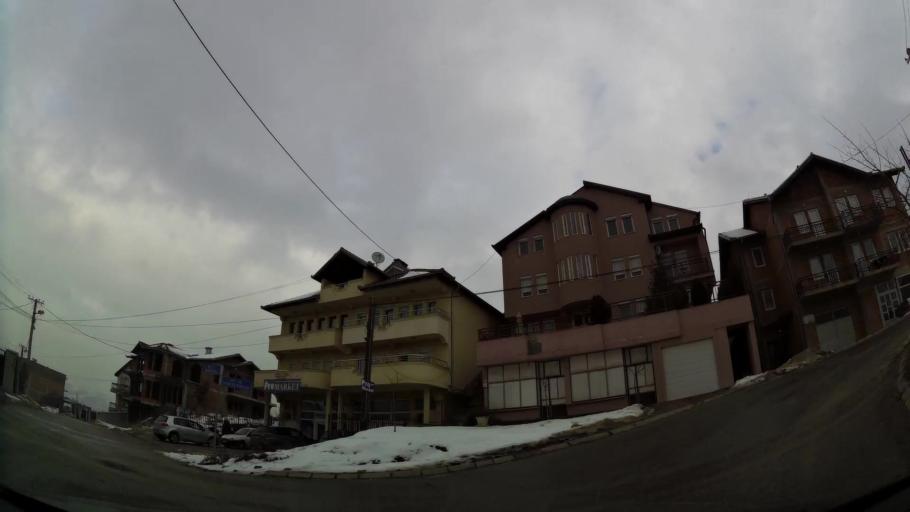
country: XK
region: Pristina
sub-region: Komuna e Prishtines
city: Pristina
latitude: 42.6768
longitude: 21.1830
